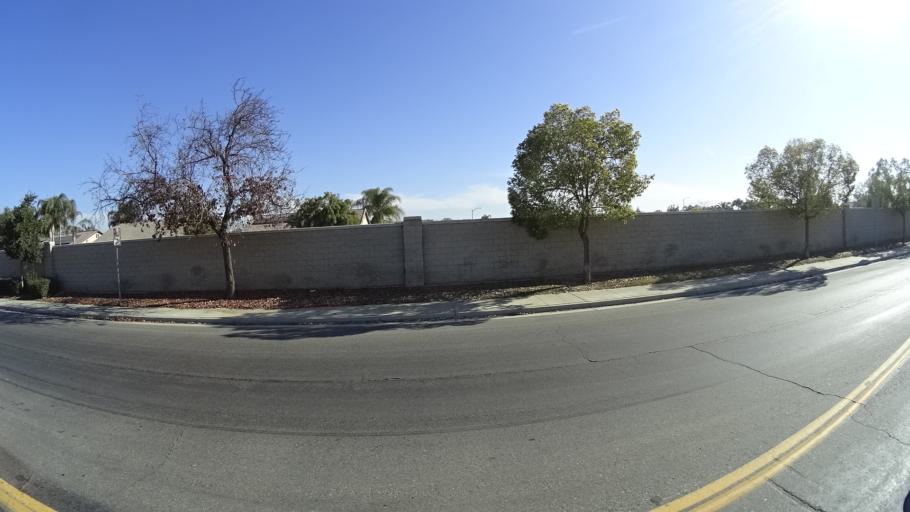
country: US
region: California
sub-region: Kern County
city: Rosedale
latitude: 35.4206
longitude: -119.1455
